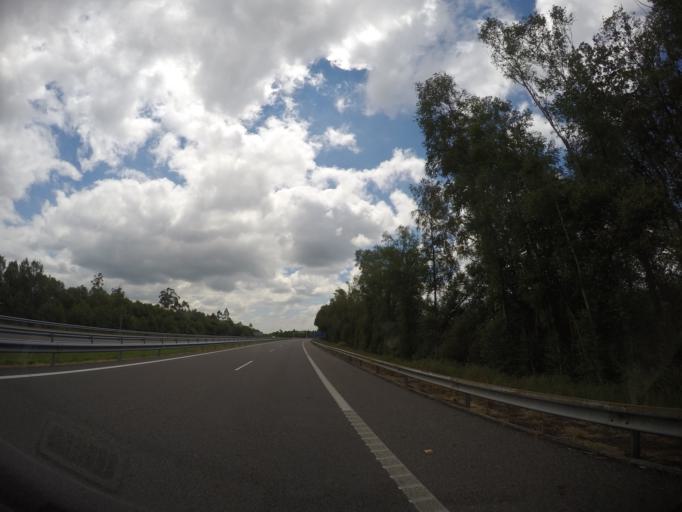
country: ES
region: Galicia
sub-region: Provincia da Coruna
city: Ordes
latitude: 43.0588
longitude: -8.3706
